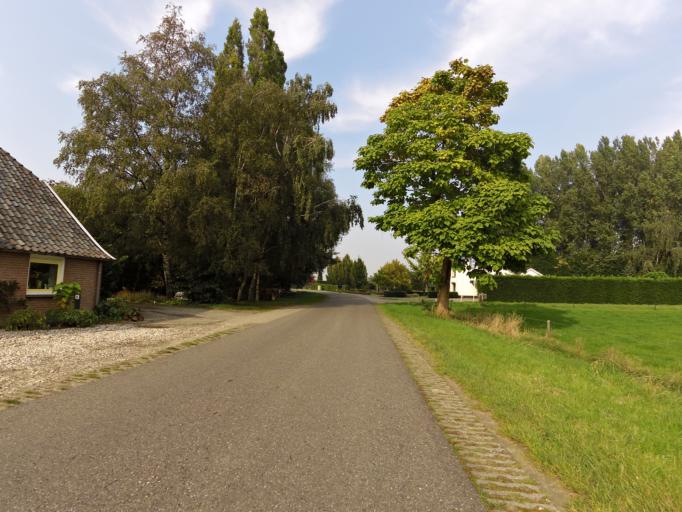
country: NL
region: Gelderland
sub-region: Gemeente Doetinchem
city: Doetinchem
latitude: 51.9475
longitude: 6.2560
